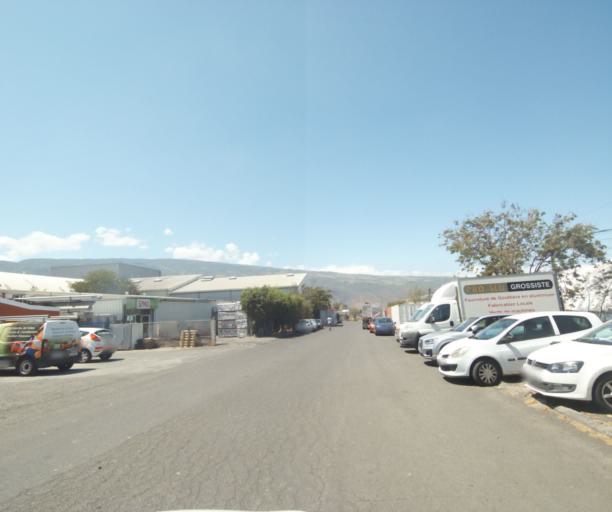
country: RE
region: Reunion
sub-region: Reunion
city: Le Port
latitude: -20.9636
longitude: 55.2981
